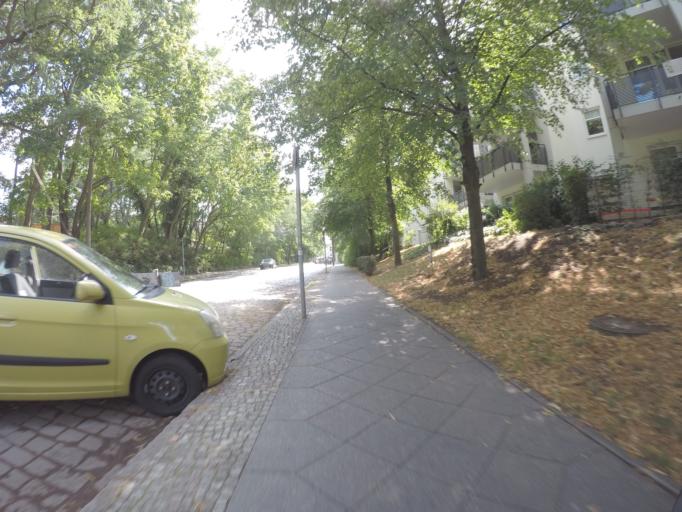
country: DE
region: Berlin
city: Friedrichsfelde
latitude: 52.5129
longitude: 13.5237
